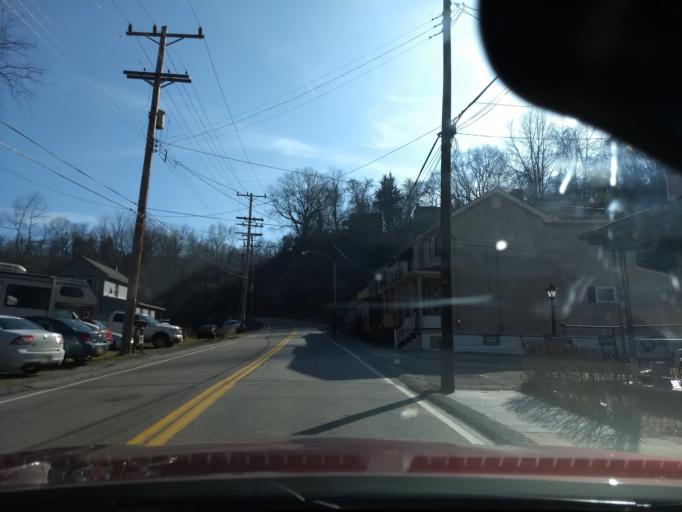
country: US
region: Pennsylvania
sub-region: Allegheny County
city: Whitaker
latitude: 40.3963
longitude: -79.8953
